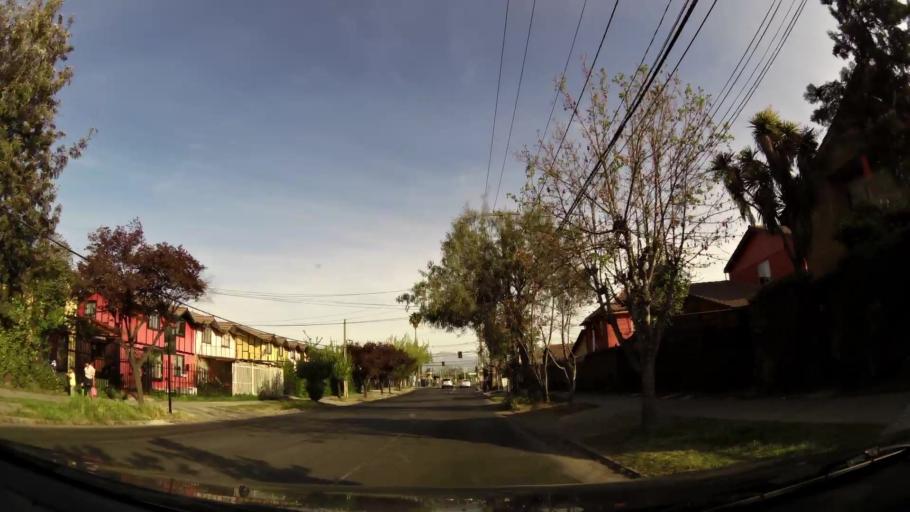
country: CL
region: Santiago Metropolitan
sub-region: Provincia de Cordillera
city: Puente Alto
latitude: -33.5794
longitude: -70.5693
